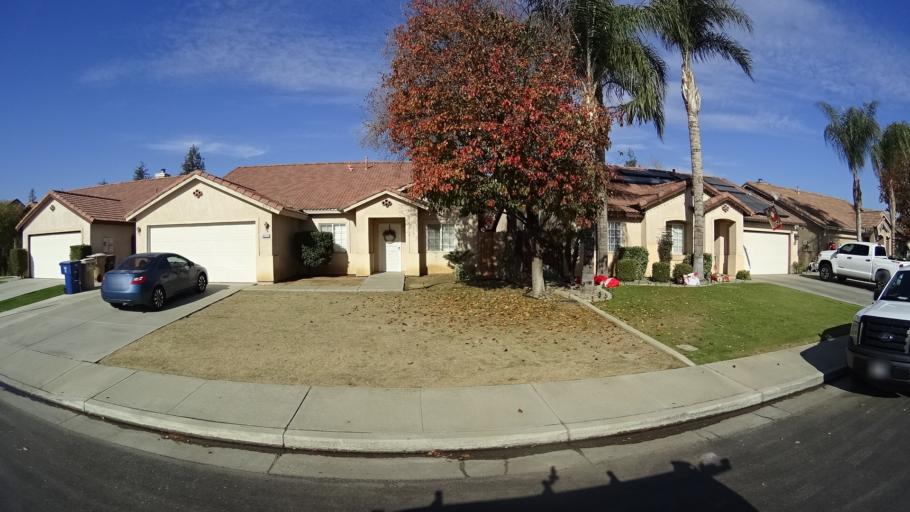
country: US
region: California
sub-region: Kern County
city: Greenacres
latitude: 35.3967
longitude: -119.0953
